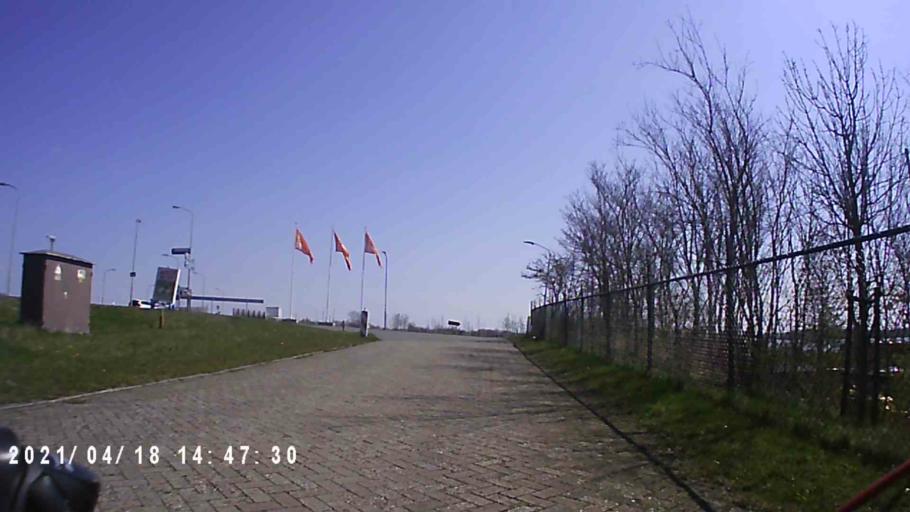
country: NL
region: Friesland
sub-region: Gemeente Dongeradeel
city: Anjum
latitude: 53.4068
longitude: 6.2005
